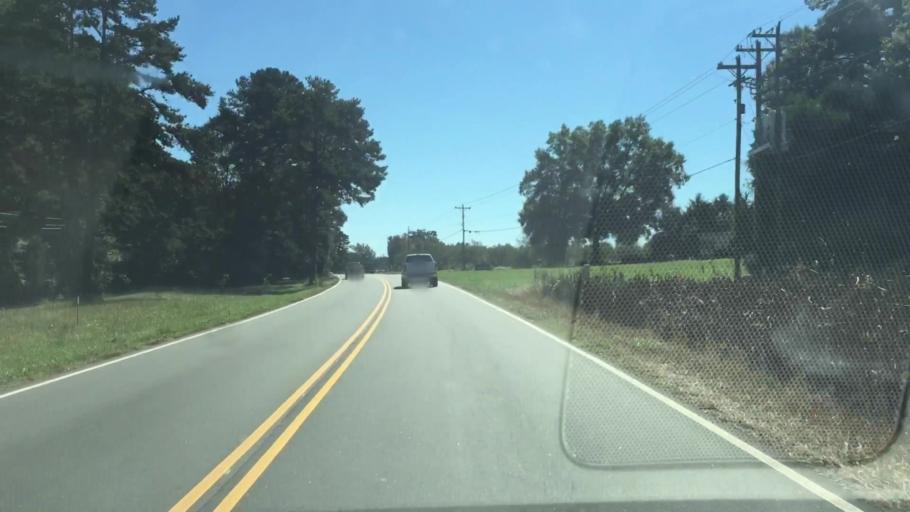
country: US
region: North Carolina
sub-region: Rowan County
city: Enochville
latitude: 35.4449
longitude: -80.7298
